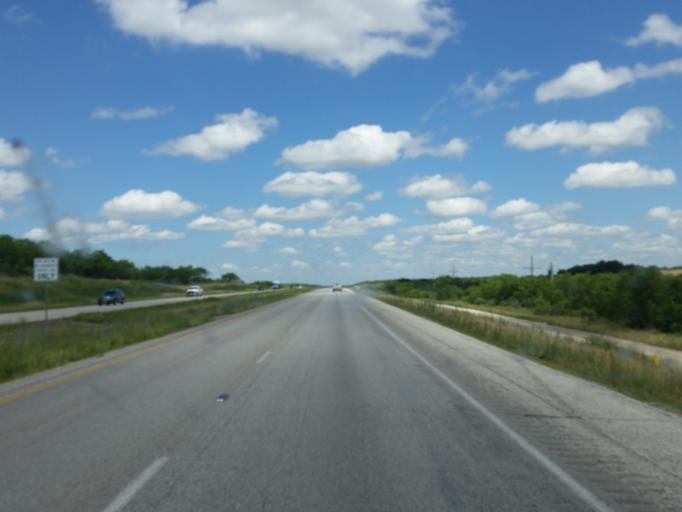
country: US
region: Texas
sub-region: Callahan County
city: Baird
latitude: 32.3831
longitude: -99.2818
